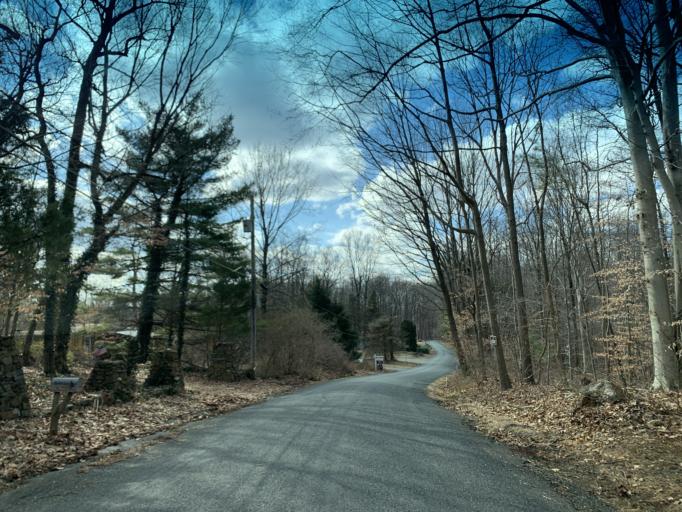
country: US
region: Maryland
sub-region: Harford County
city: Riverside
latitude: 39.5104
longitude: -76.2388
